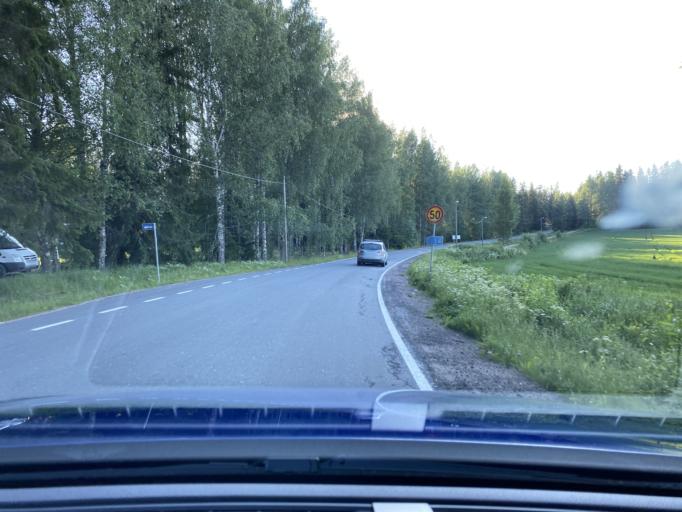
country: FI
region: Haeme
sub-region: Riihimaeki
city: Riihimaeki
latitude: 60.7248
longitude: 24.6999
